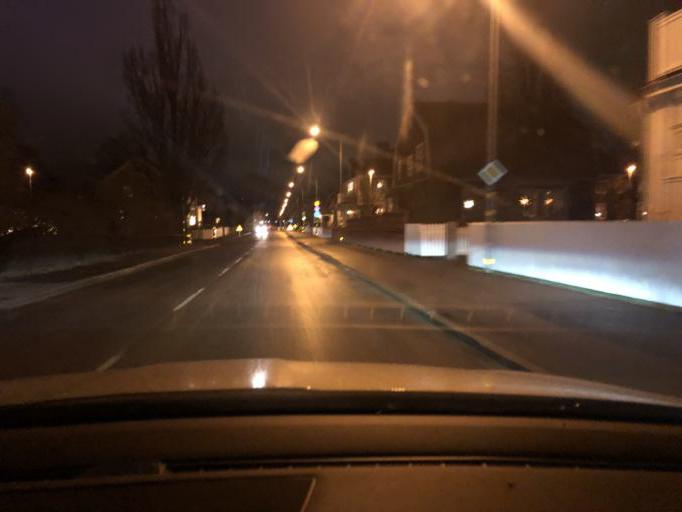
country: SE
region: Vaermland
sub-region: Karlstads Kommun
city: Karlstad
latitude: 59.3741
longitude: 13.4846
